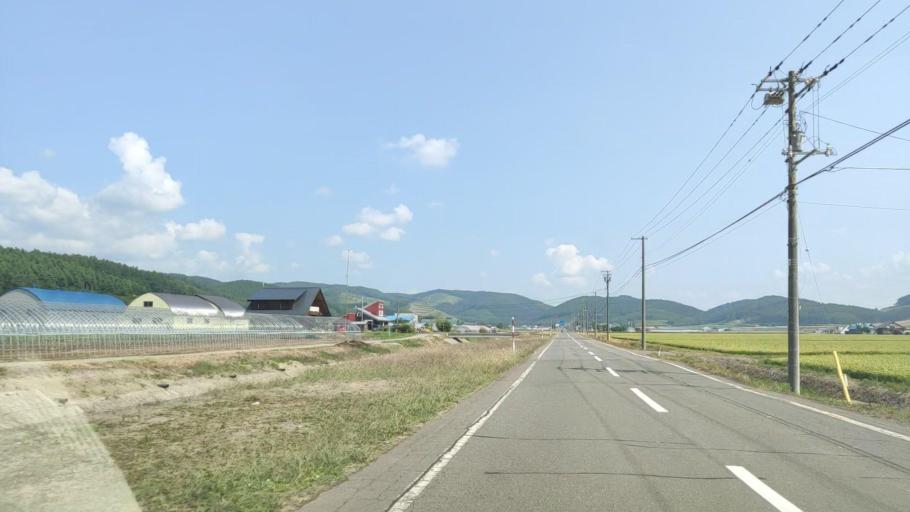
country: JP
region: Hokkaido
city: Shimo-furano
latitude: 43.3985
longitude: 142.3927
